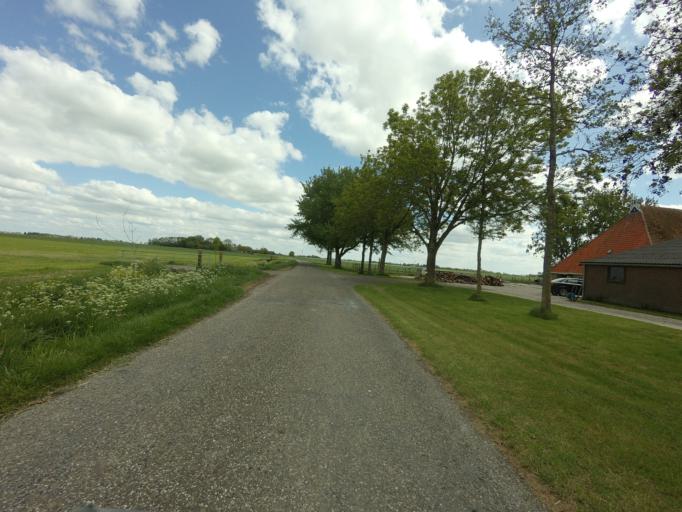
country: NL
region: Friesland
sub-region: Gemeente Franekeradeel
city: Tzum
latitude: 53.1366
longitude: 5.5581
